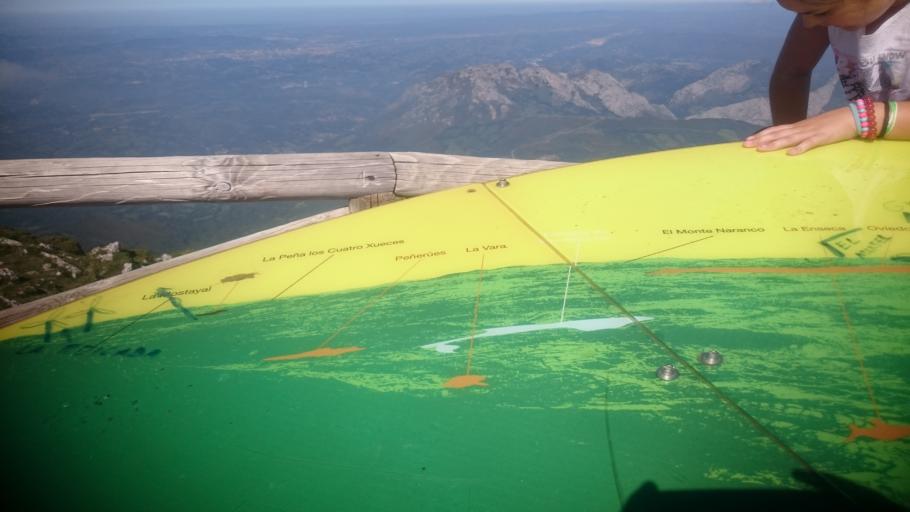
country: ES
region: Asturias
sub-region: Province of Asturias
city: Castandiello
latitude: 43.2268
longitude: -5.9362
